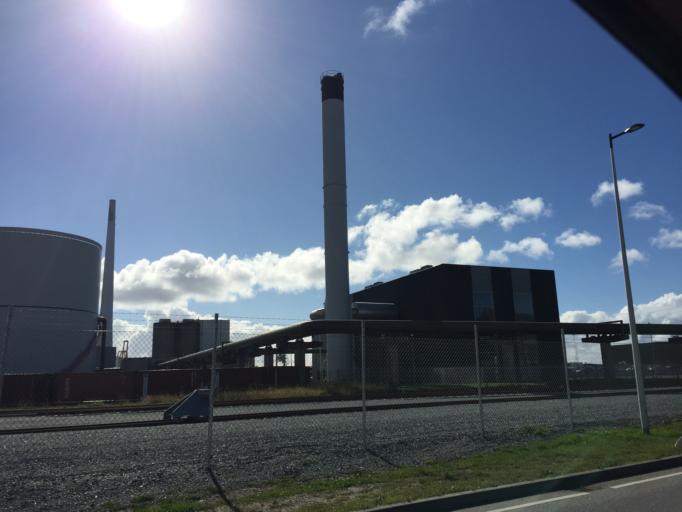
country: DK
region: South Denmark
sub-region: Esbjerg Kommune
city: Esbjerg
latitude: 55.4620
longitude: 8.4577
